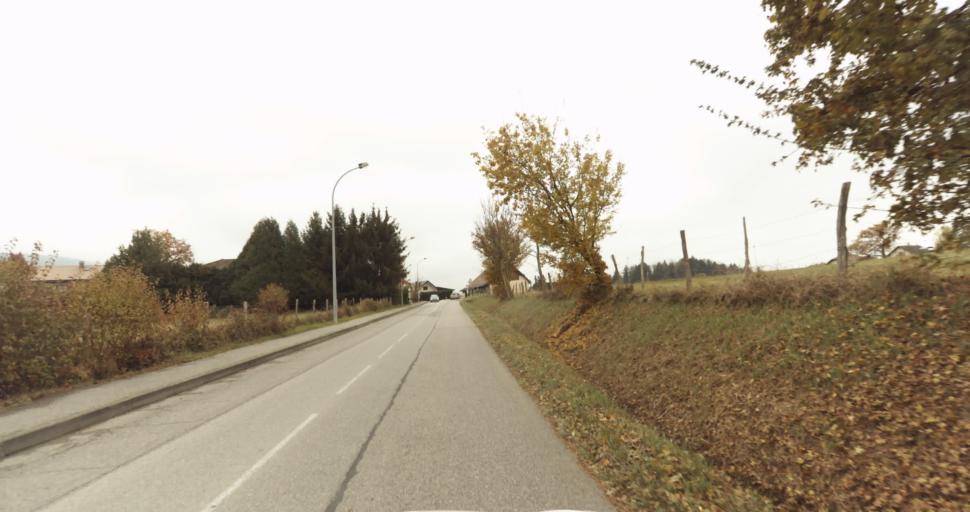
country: FR
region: Rhone-Alpes
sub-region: Departement de la Haute-Savoie
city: Seynod
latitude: 45.8721
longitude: 6.0861
